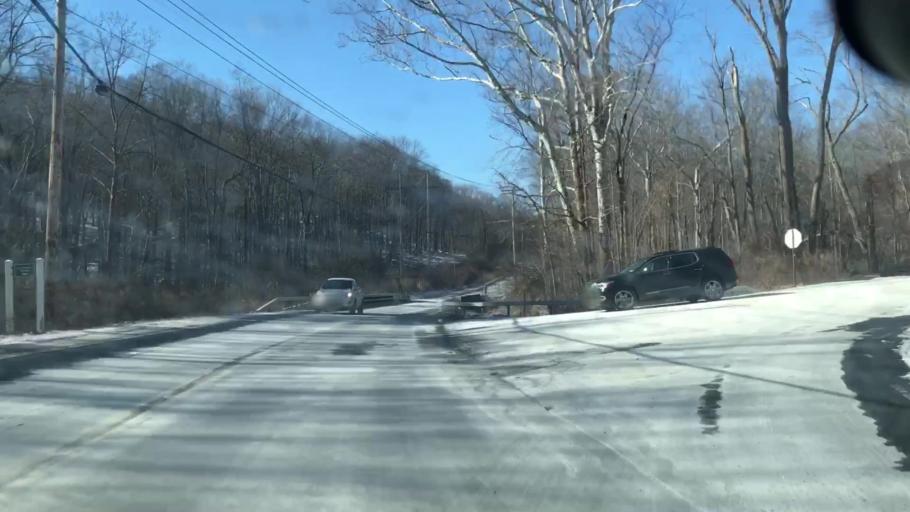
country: US
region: New York
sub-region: Putnam County
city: Carmel Hamlet
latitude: 41.3883
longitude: -73.6826
